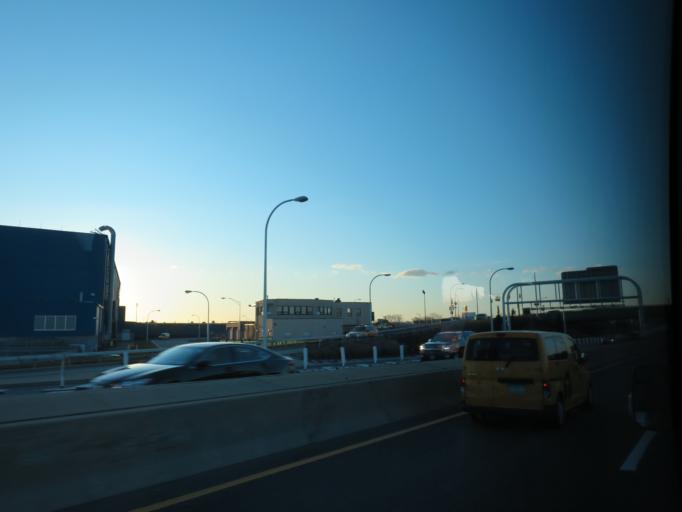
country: US
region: New York
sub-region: Queens County
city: Jamaica
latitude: 40.6546
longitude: -73.7885
